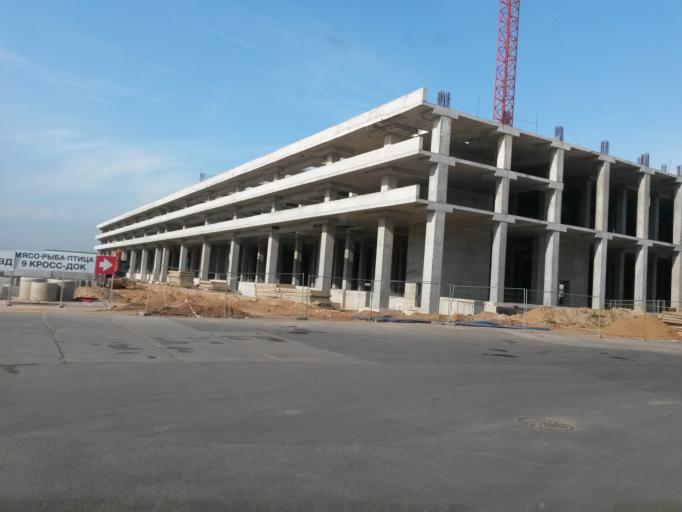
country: RU
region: Moskovskaya
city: Mosrentgen
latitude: 55.6012
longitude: 37.4648
